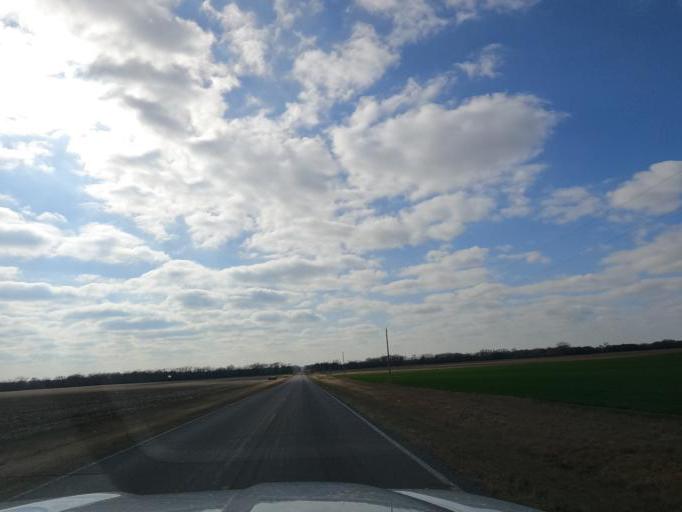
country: US
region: Kansas
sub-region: McPherson County
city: Inman
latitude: 38.2320
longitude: -97.8551
